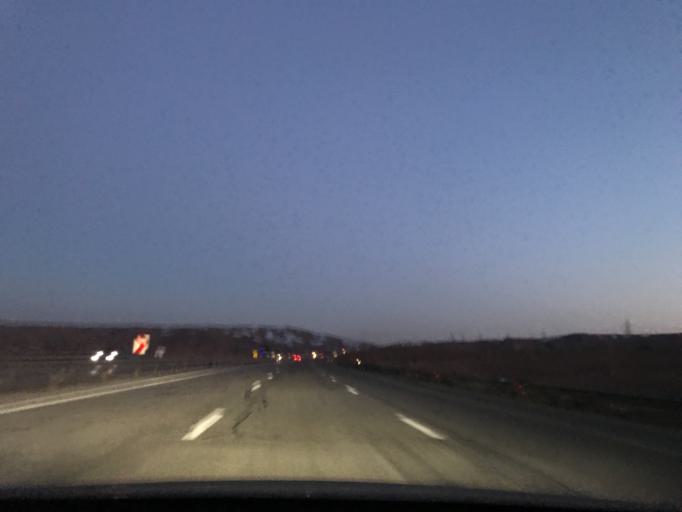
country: IR
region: Isfahan
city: Kashan
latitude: 33.8227
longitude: 51.6300
